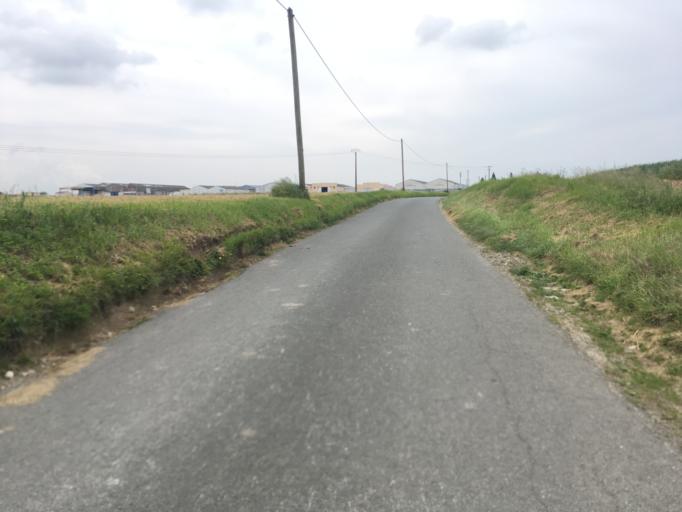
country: FR
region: Poitou-Charentes
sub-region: Departement de la Charente-Maritime
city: Aytre
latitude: 46.1444
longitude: -1.1215
